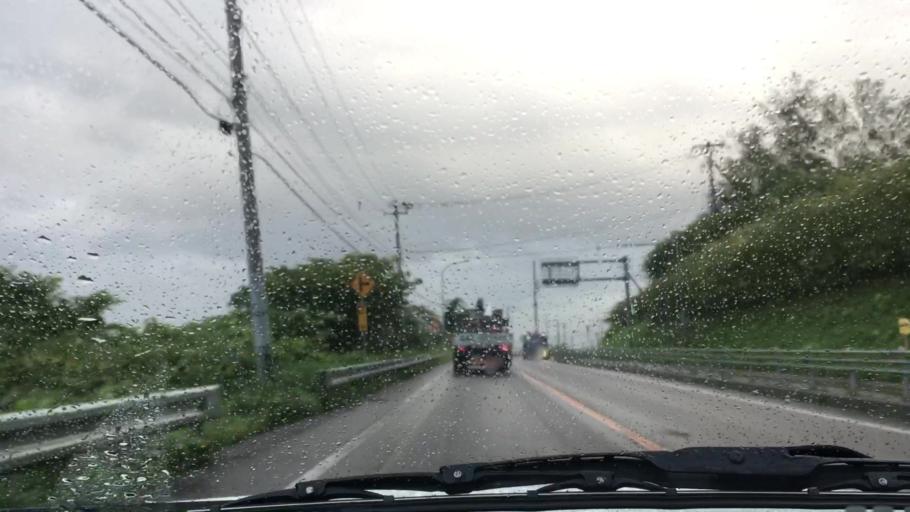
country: JP
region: Hokkaido
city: Nanae
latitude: 42.1559
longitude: 140.4804
